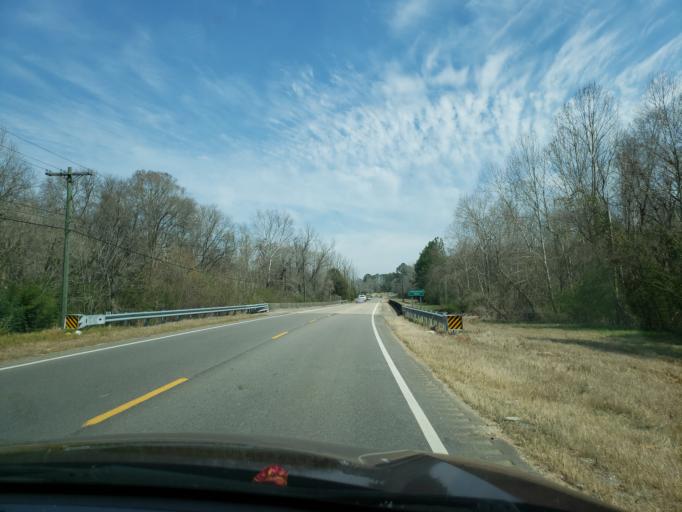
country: US
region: Alabama
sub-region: Elmore County
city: Eclectic
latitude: 32.5803
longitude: -86.0889
